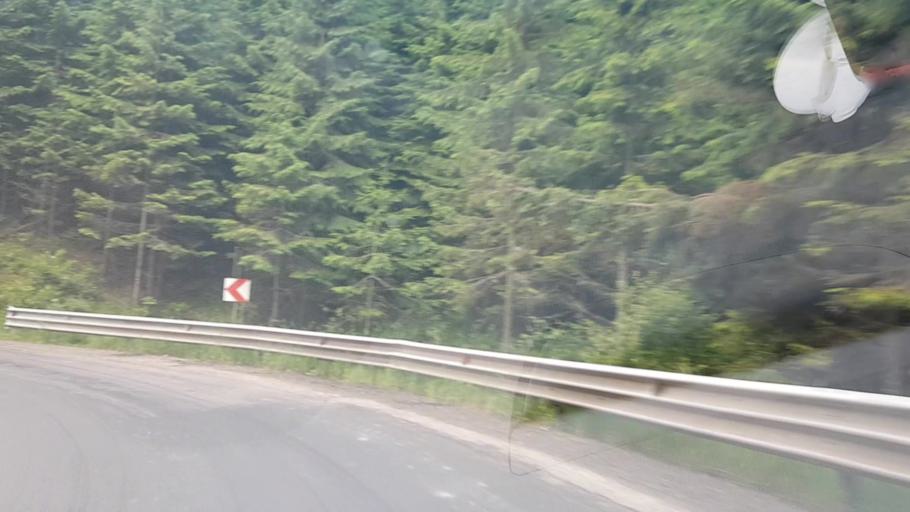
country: RO
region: Harghita
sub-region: Comuna Varsag
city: Varsag
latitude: 46.6647
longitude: 25.3035
